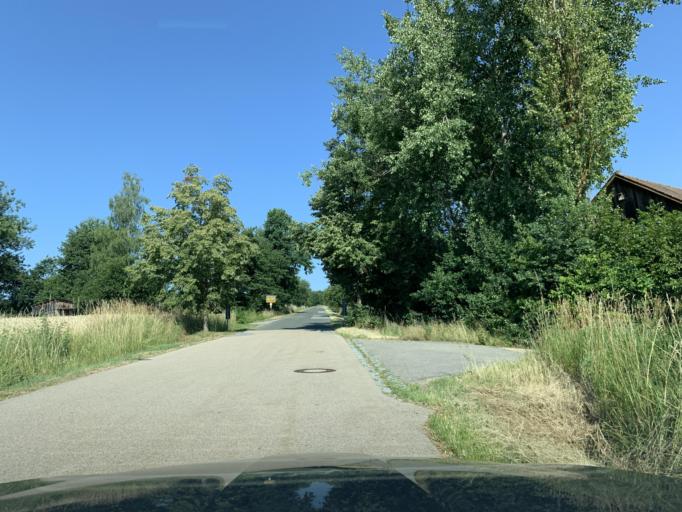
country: DE
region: Bavaria
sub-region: Upper Palatinate
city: Schwarzhofen
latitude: 49.3848
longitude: 12.3243
